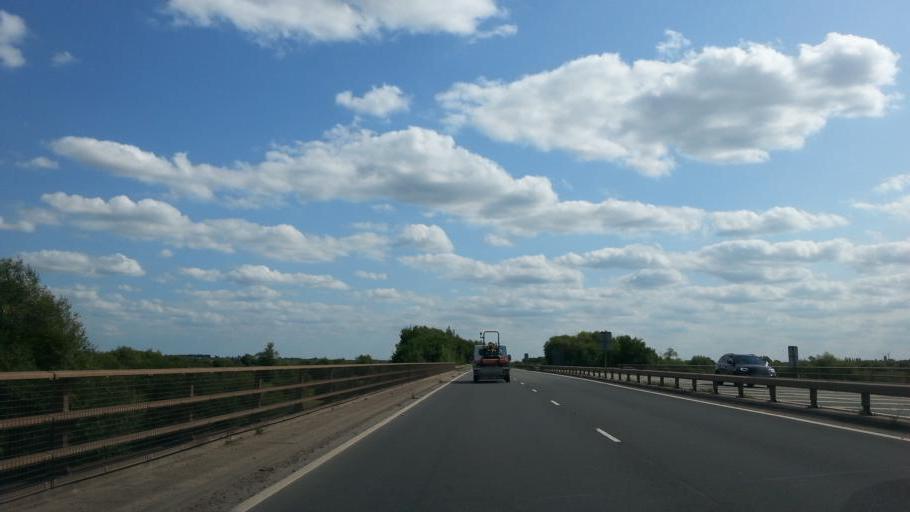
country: GB
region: England
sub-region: Leicestershire
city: Barrow upon Soar
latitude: 52.7398
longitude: -1.1432
